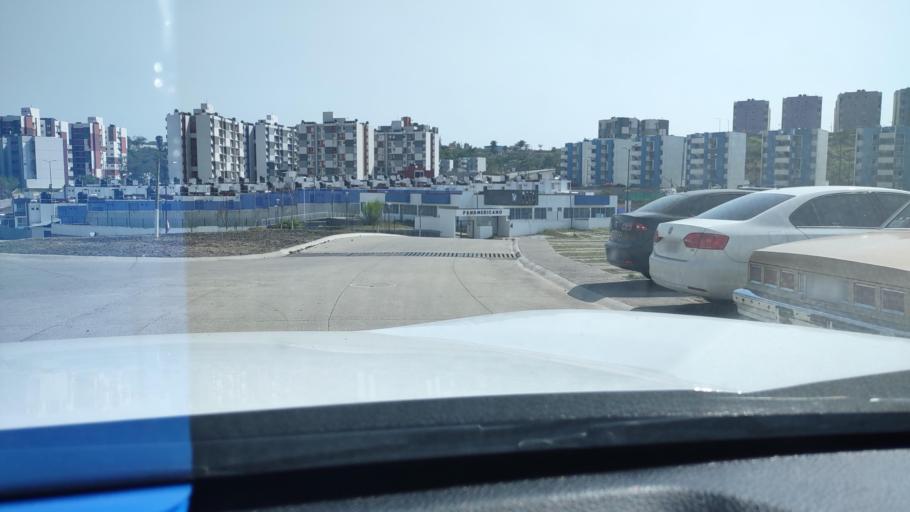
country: MX
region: Veracruz
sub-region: Emiliano Zapata
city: Las Trancas
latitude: 19.5150
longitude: -96.8486
